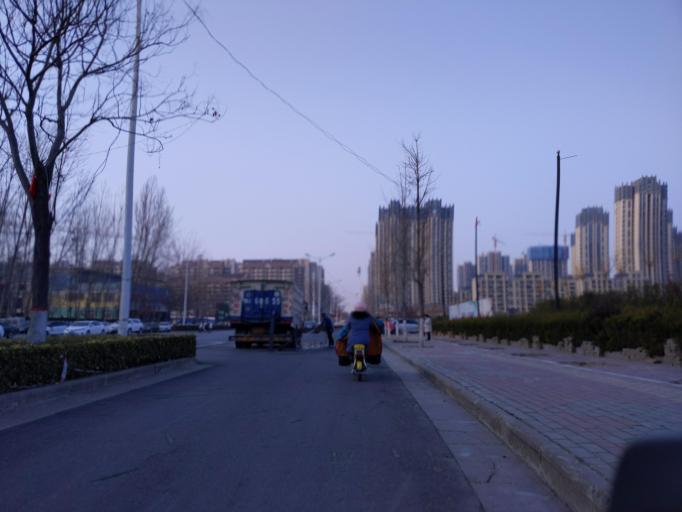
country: CN
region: Henan Sheng
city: Puyang
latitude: 35.7841
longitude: 115.0151
